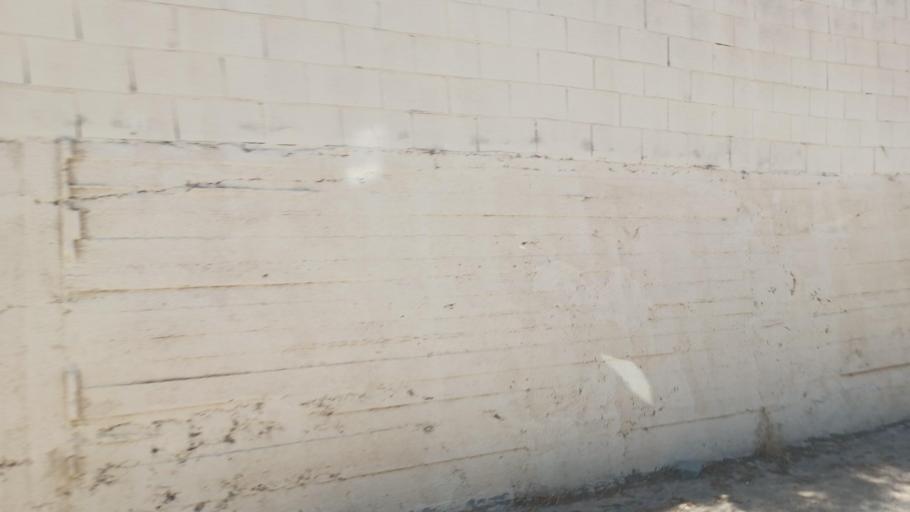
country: CY
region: Ammochostos
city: Avgorou
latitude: 35.0626
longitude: 33.8513
